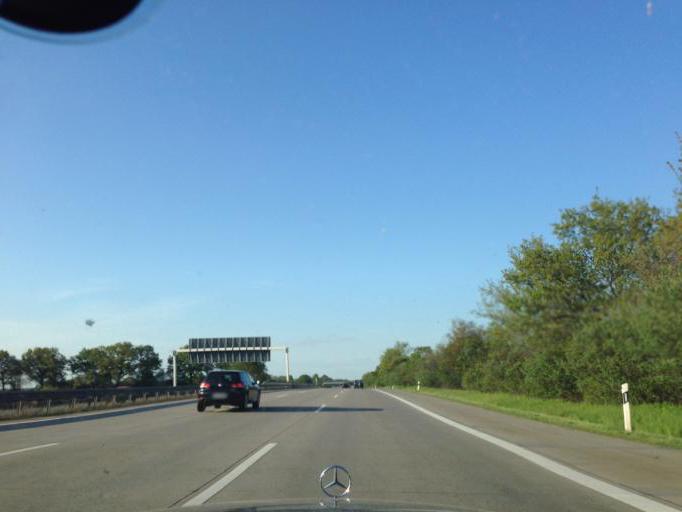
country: DE
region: Schleswig-Holstein
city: Lasbek
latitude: 53.7258
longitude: 10.3452
